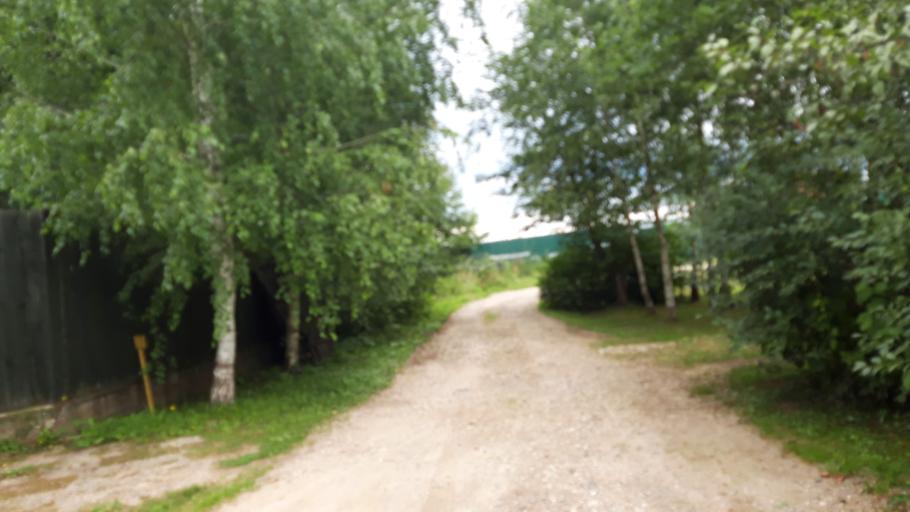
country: RU
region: Tverskaya
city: Konakovo
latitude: 56.6752
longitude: 36.7202
